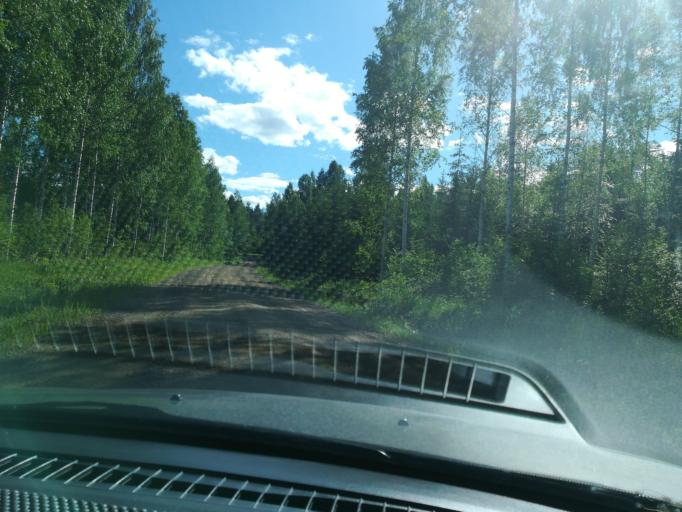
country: FI
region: Southern Savonia
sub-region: Mikkeli
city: Puumala
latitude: 61.6647
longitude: 28.1442
